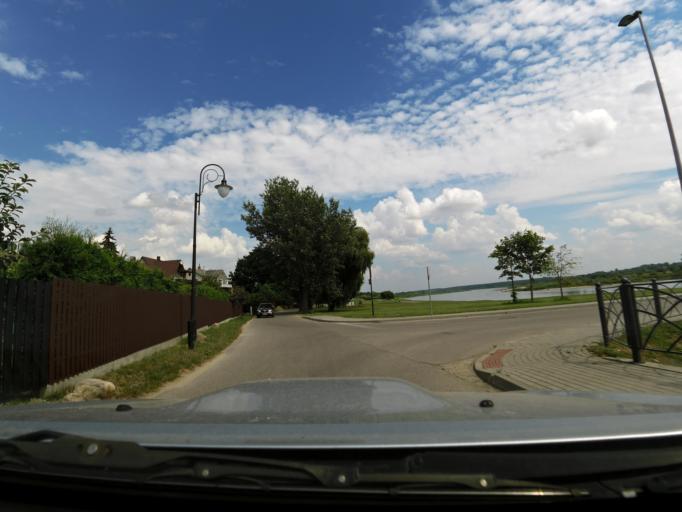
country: LT
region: Taurages apskritis
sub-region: Jurbarkas
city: Jurbarkas
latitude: 55.0768
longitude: 22.7750
